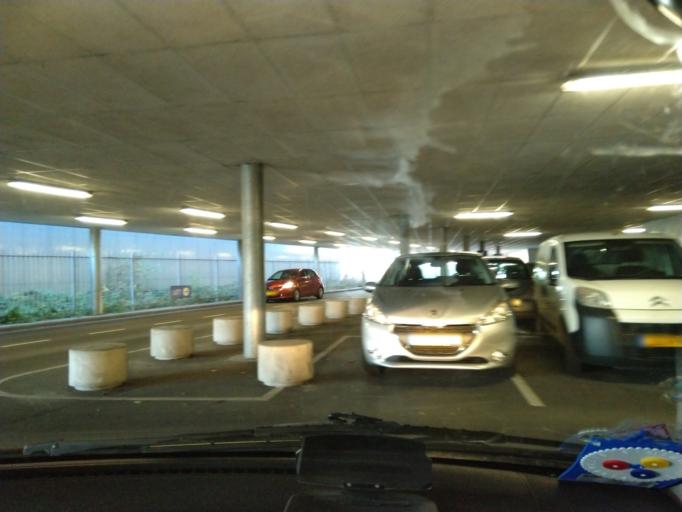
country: NL
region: Groningen
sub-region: Gemeente Groningen
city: Oosterpark
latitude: 53.2172
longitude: 6.5894
